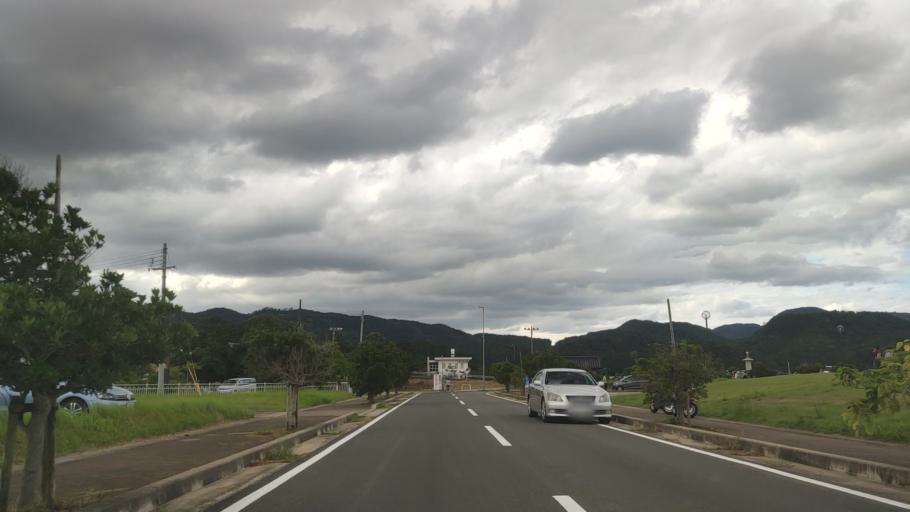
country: JP
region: Hyogo
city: Toyooka
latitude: 35.6077
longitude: 134.8987
